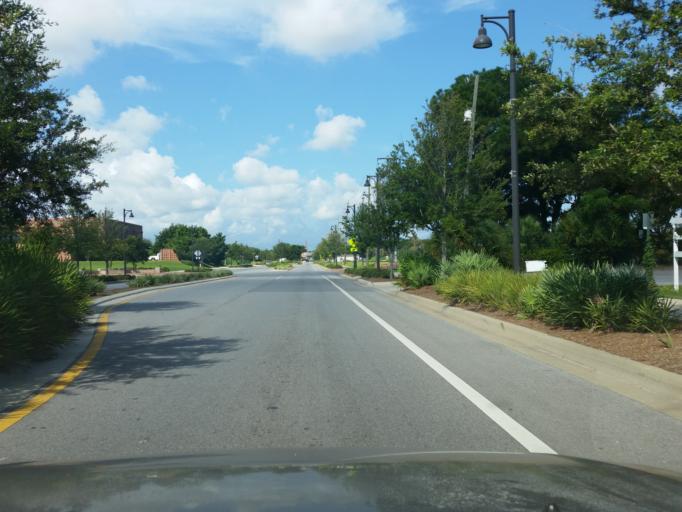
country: US
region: Florida
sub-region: Escambia County
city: Pensacola
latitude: 30.4065
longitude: -87.2197
